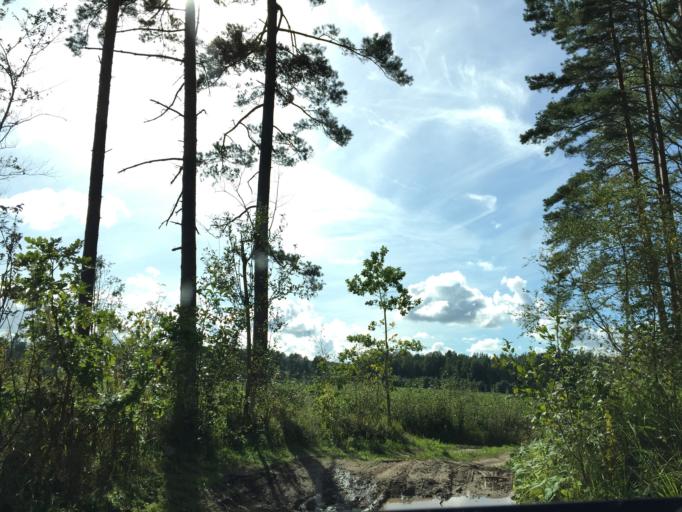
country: LV
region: Kuldigas Rajons
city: Kuldiga
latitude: 56.9921
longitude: 21.8101
